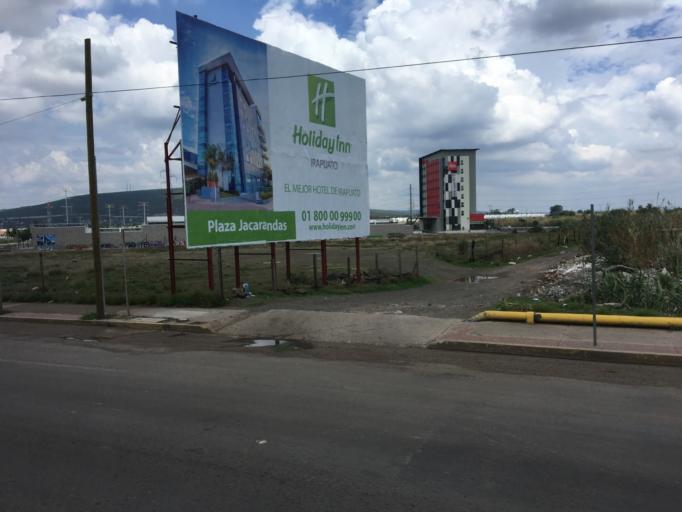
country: MX
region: Guanajuato
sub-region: Irapuato
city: Ex-Hacienda del Copal
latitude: 20.7214
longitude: -101.3468
